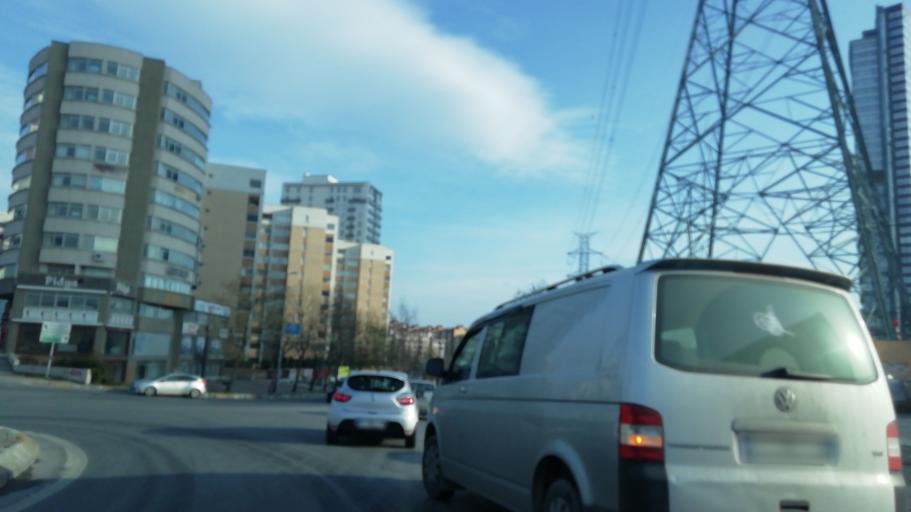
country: TR
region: Istanbul
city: Esenyurt
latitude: 41.0643
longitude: 28.6659
